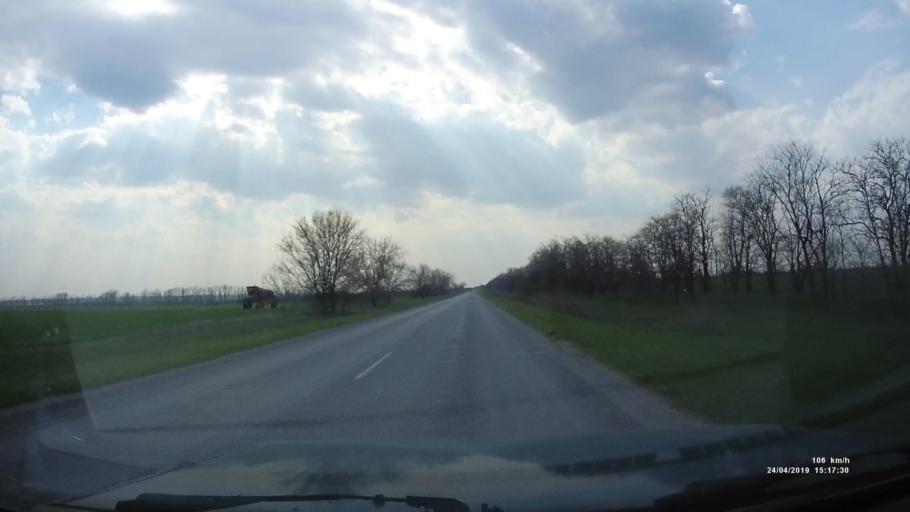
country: RU
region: Rostov
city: Remontnoye
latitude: 46.5465
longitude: 43.1883
